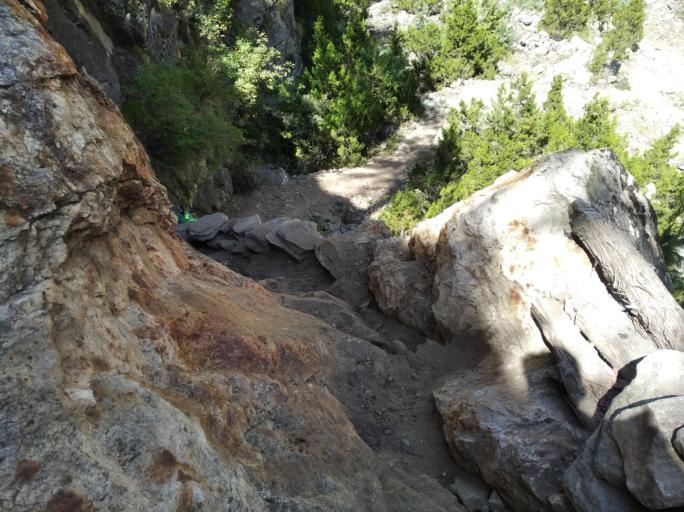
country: NP
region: Western Region
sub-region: Dhawalagiri Zone
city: Jomsom
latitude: 28.8955
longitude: 83.0670
